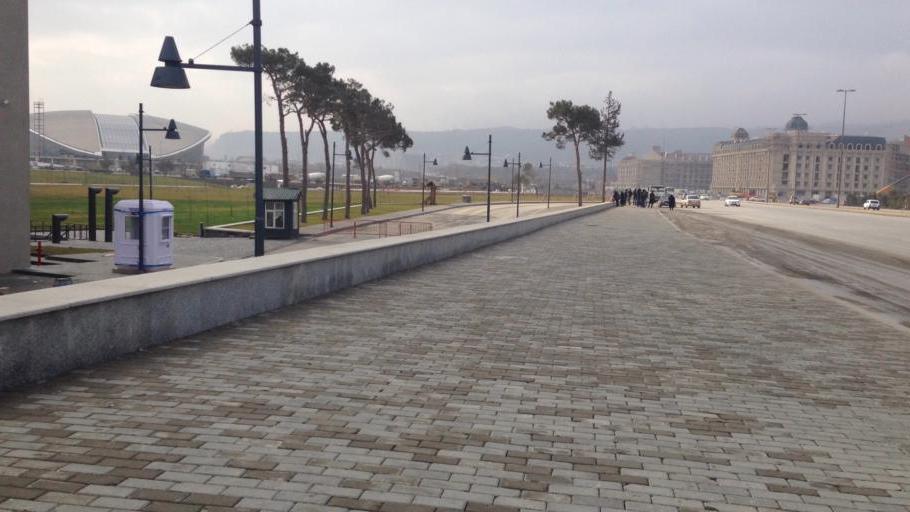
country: AZ
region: Baki
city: Badamdar
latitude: 40.3398
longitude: 49.8374
